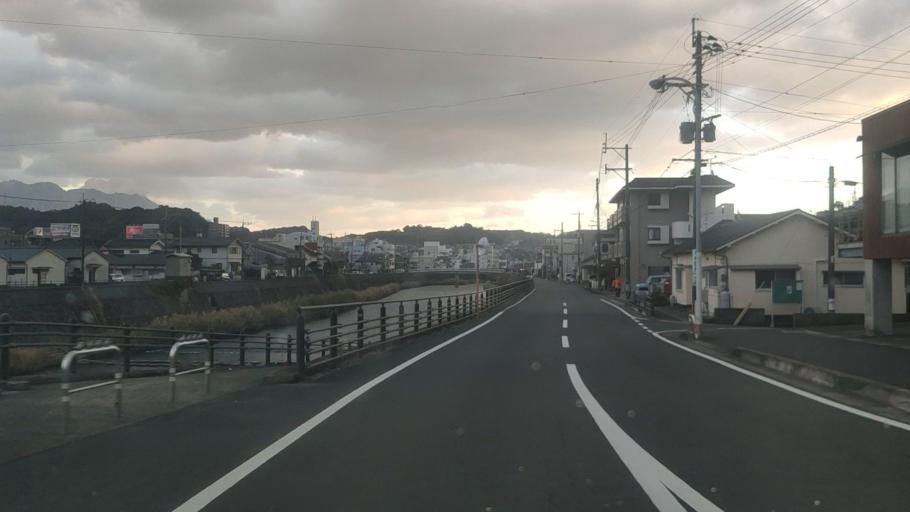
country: JP
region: Kagoshima
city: Kagoshima-shi
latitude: 31.6129
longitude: 130.5292
